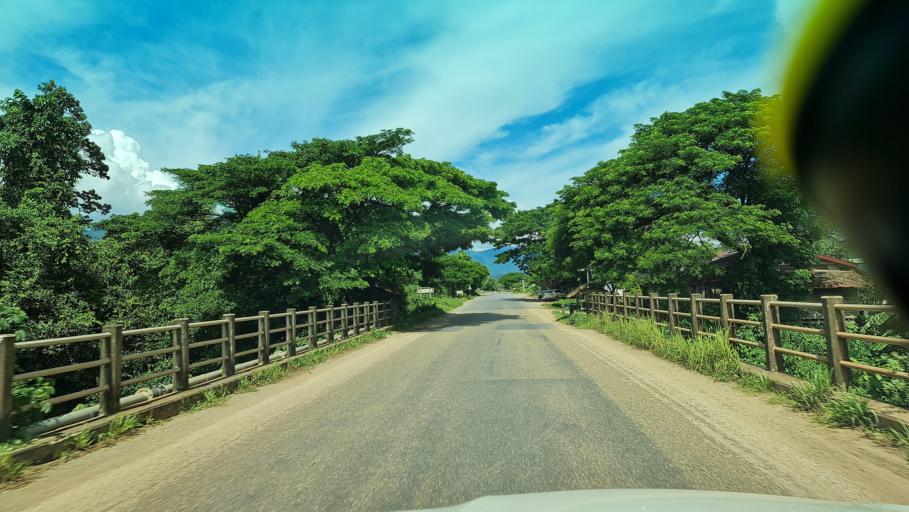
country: LA
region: Bolikhamxai
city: Pakkading
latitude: 18.2992
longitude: 104.1022
